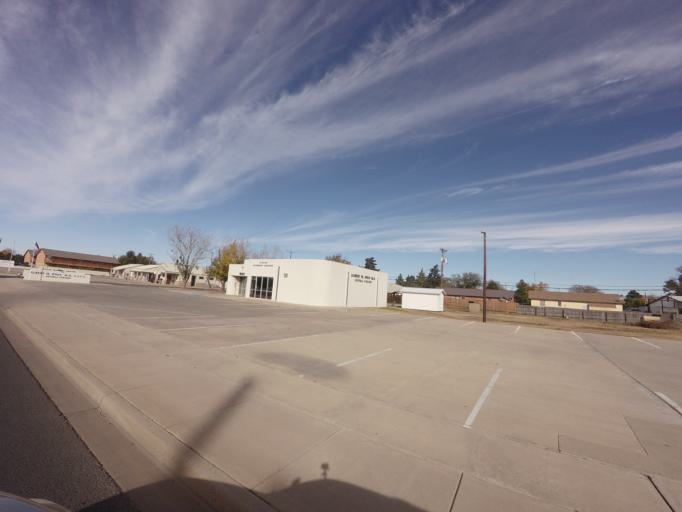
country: US
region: New Mexico
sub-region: Curry County
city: Clovis
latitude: 34.4194
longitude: -103.2268
